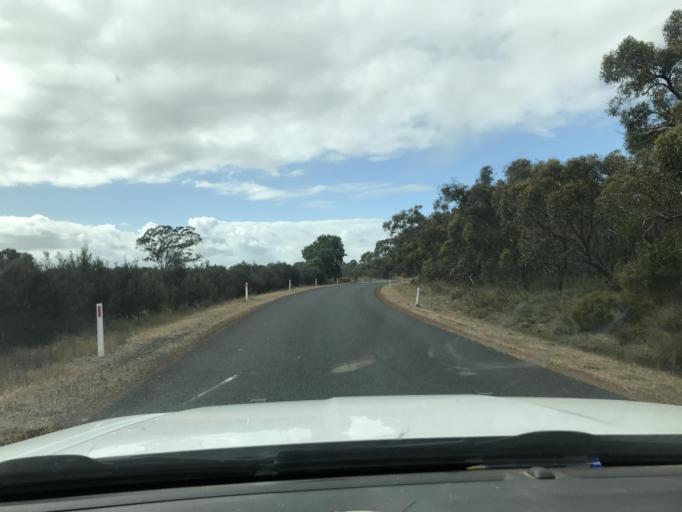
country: AU
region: South Australia
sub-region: Wattle Range
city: Penola
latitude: -37.1724
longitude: 141.2716
